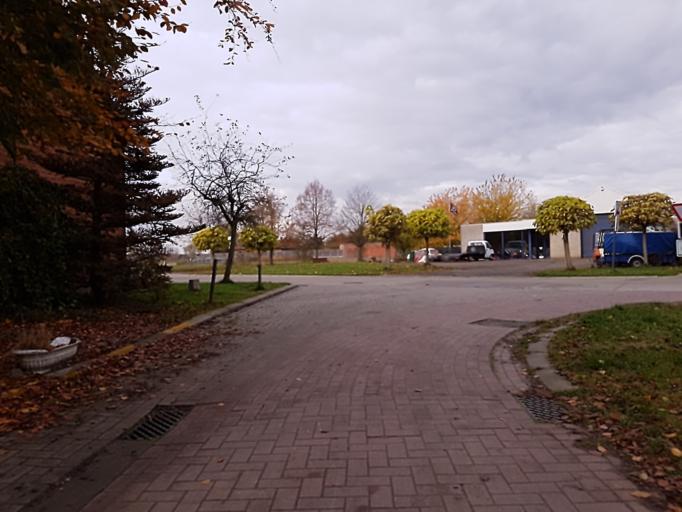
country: BE
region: Flanders
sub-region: Provincie Antwerpen
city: Ranst
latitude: 51.1876
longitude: 4.5505
